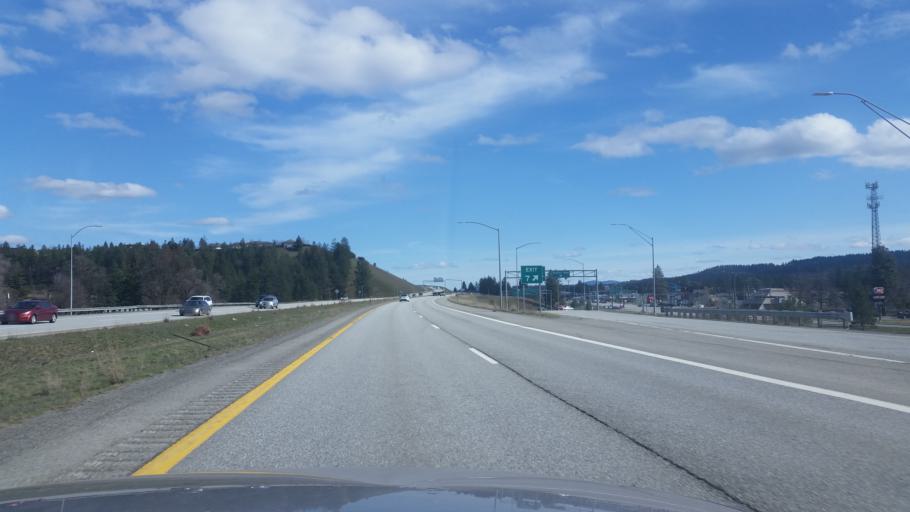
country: US
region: Idaho
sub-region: Kootenai County
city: Post Falls
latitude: 47.7120
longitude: -116.9021
